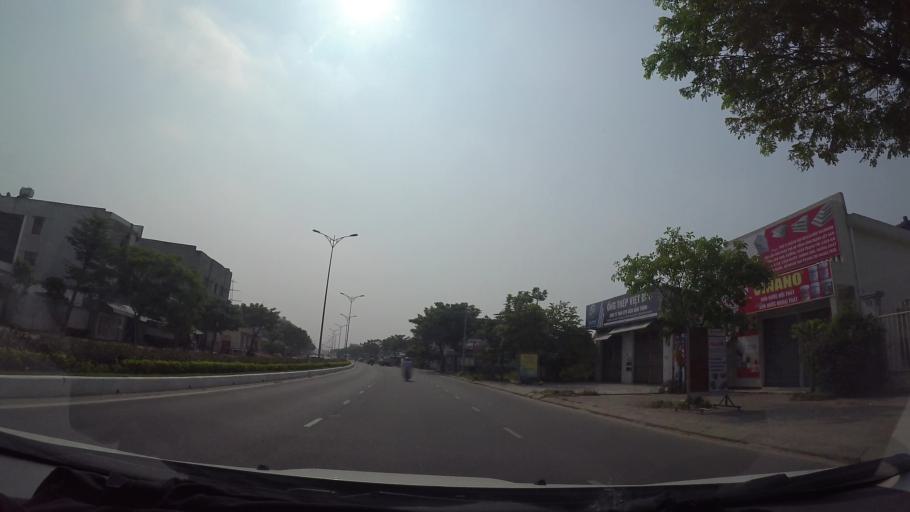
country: VN
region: Da Nang
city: Cam Le
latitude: 16.0053
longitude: 108.2217
